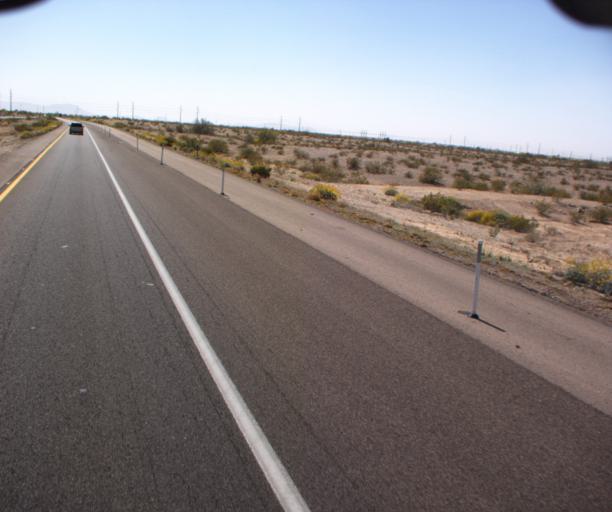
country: US
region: Arizona
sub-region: Maricopa County
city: Gila Bend
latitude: 32.9808
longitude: -112.6686
